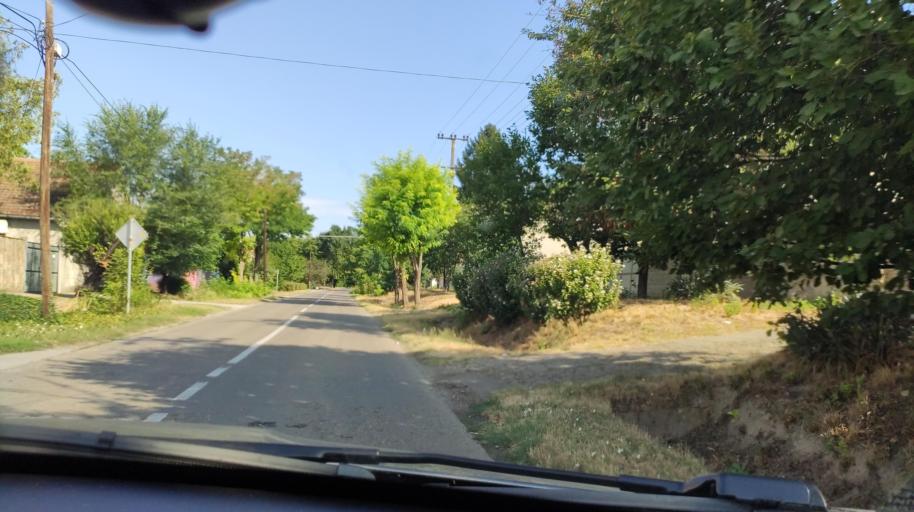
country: RS
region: Autonomna Pokrajina Vojvodina
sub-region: Severnobacki Okrug
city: Backa Topola
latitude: 45.8077
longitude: 19.6250
